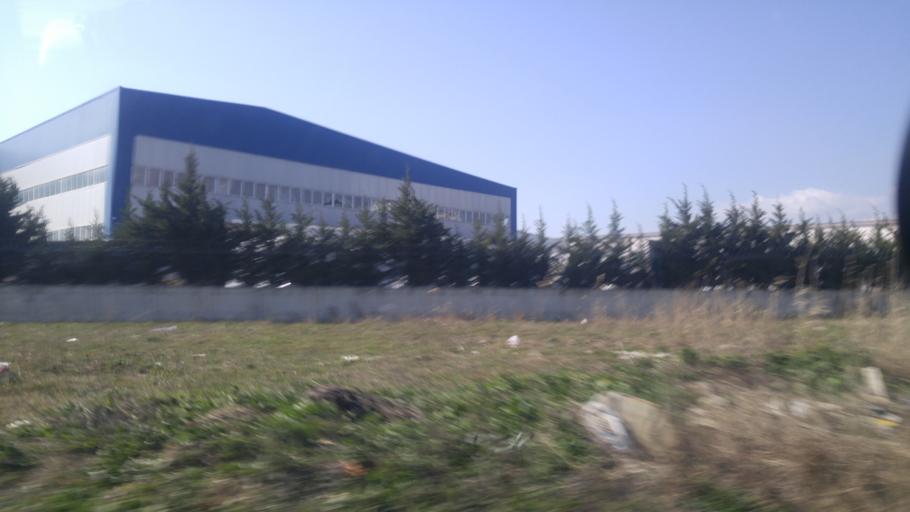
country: TR
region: Istanbul
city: Canta
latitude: 41.0740
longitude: 28.1058
